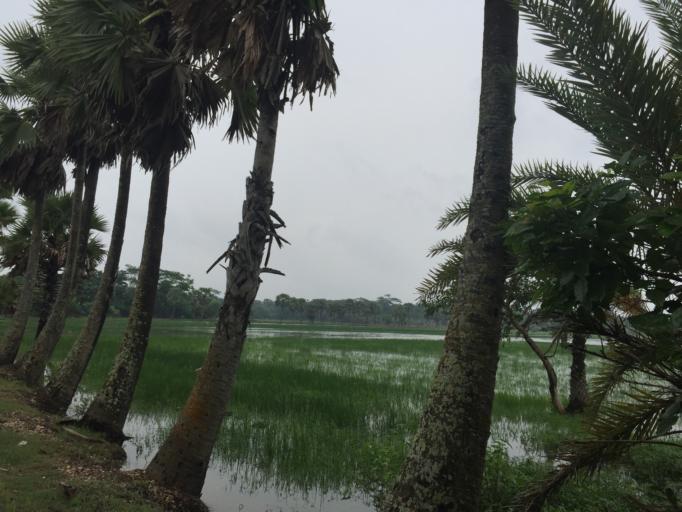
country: BD
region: Barisal
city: Mathba
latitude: 22.2111
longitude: 89.9276
